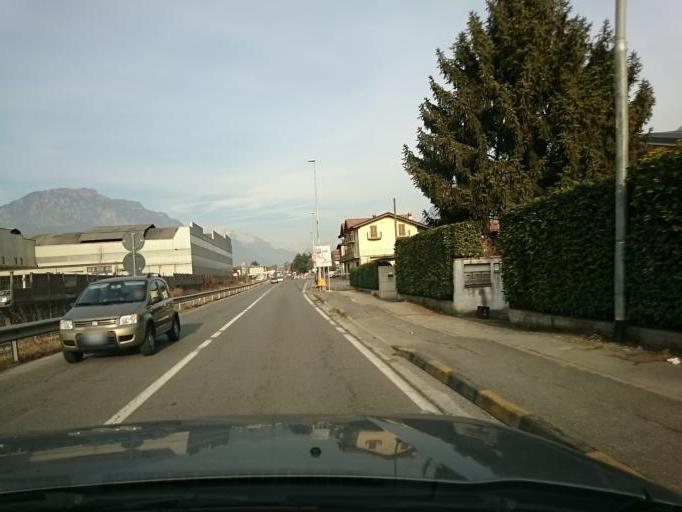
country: IT
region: Lombardy
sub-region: Provincia di Brescia
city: Pian Camuno
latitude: 45.8426
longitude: 10.1418
